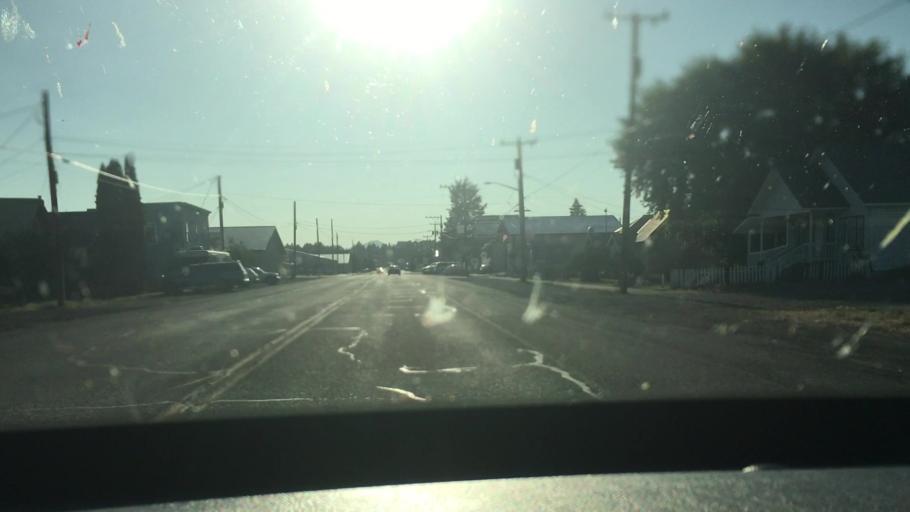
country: US
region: Washington
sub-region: Kittitas County
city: Cle Elum
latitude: 47.1932
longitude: -120.9241
